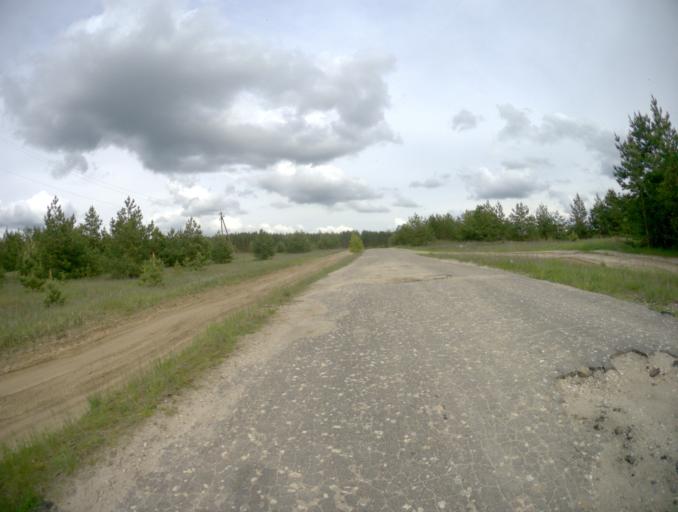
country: RU
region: Rjazan
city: Gus'-Zheleznyy
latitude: 55.0104
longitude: 41.1747
